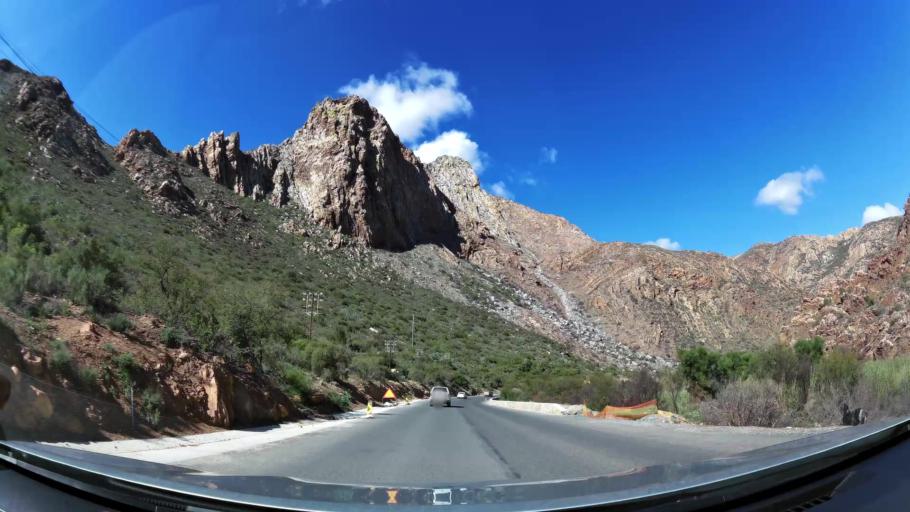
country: ZA
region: Western Cape
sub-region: Cape Winelands District Municipality
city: Ashton
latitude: -33.7991
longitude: 20.1047
